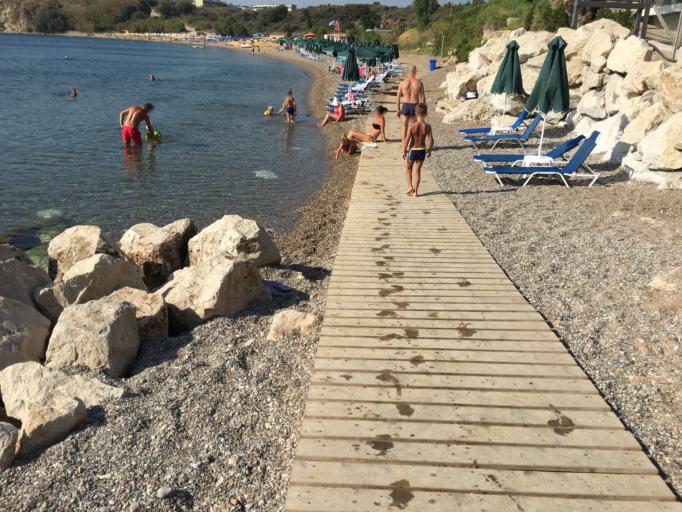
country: GR
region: South Aegean
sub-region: Nomos Dodekanisou
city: Rodos
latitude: 36.4061
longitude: 28.2288
